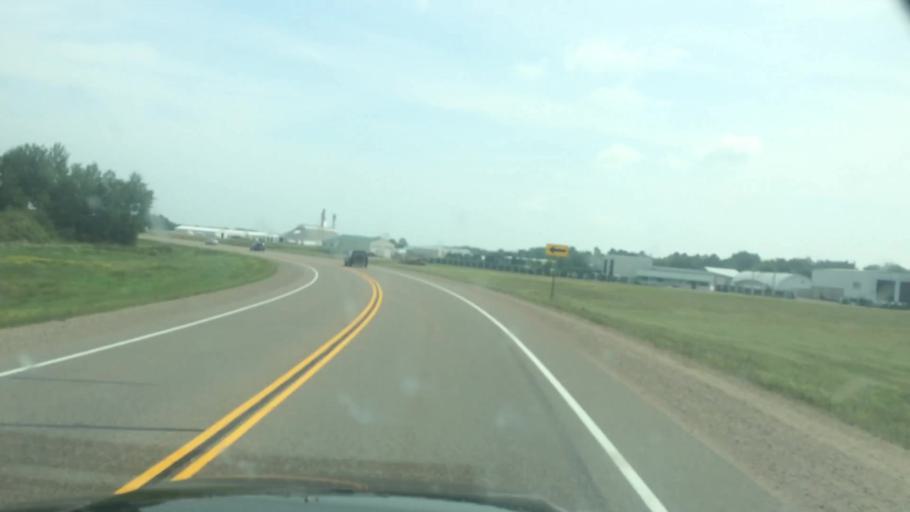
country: US
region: Wisconsin
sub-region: Langlade County
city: Antigo
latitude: 45.1558
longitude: -89.1646
